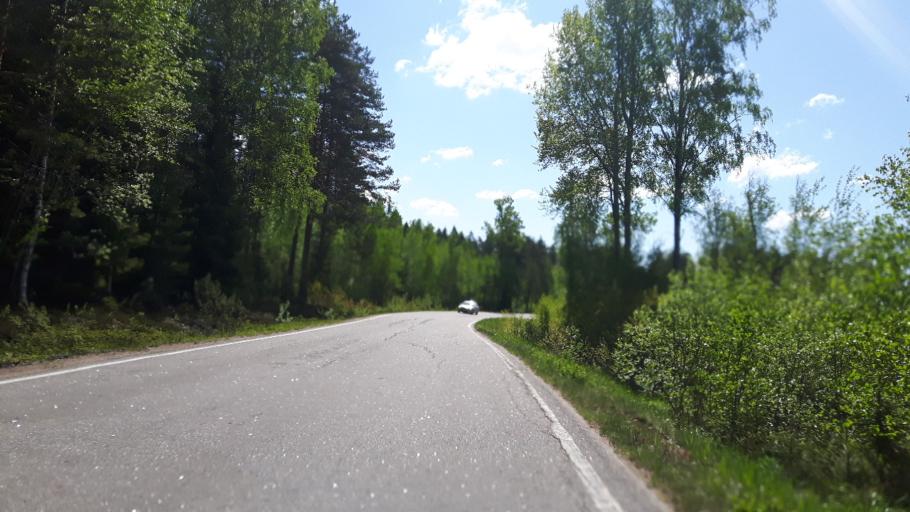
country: FI
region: Kymenlaakso
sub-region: Kotka-Hamina
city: Hamina
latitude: 60.5292
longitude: 27.2940
